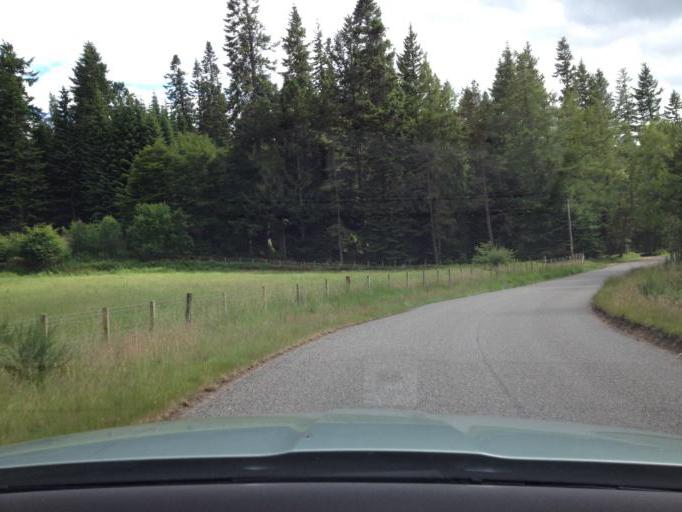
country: GB
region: Scotland
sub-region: Aberdeenshire
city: Banchory
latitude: 57.0034
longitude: -2.5684
